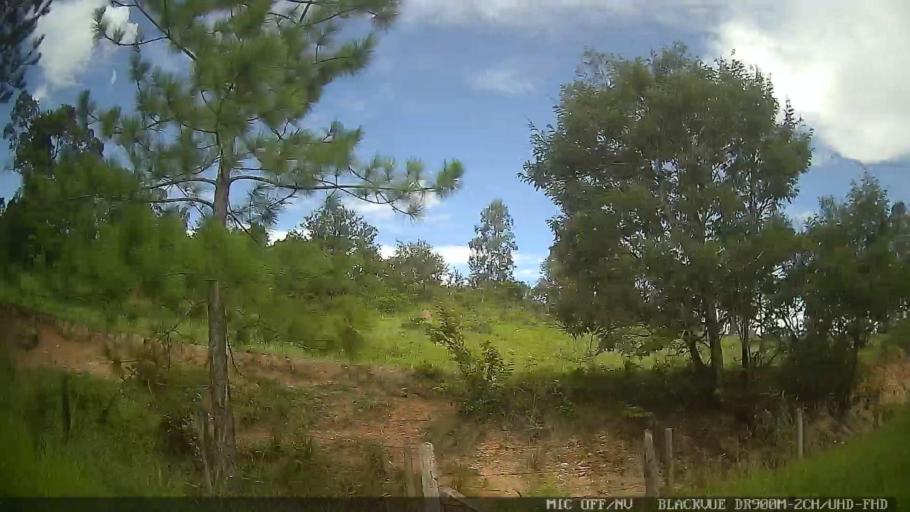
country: BR
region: Sao Paulo
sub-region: Conchas
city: Conchas
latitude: -22.9972
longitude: -47.9997
